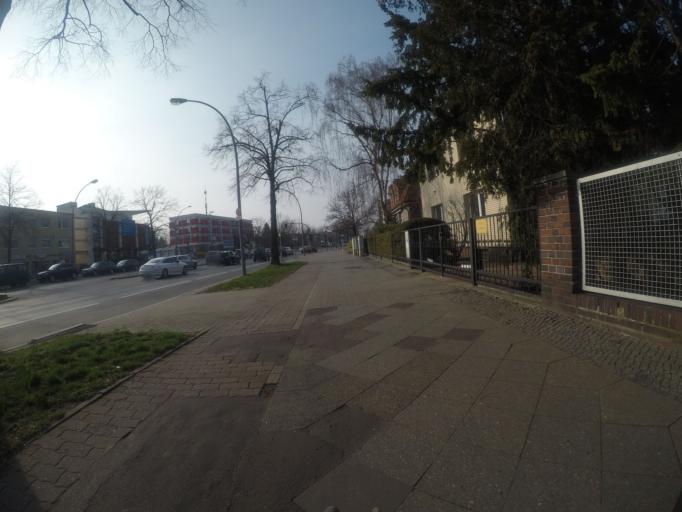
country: DE
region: Berlin
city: Gropiusstadt
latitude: 52.4340
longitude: 13.4701
